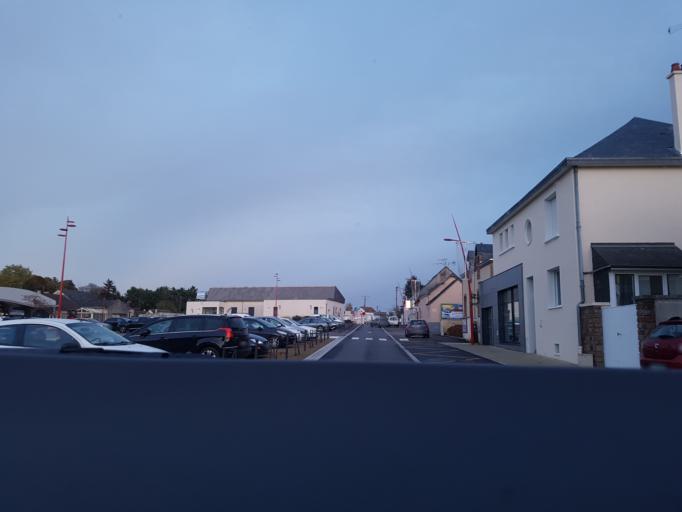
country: FR
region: Pays de la Loire
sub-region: Departement de la Mayenne
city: Cosse-le-Vivien
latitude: 47.9444
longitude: -0.9126
